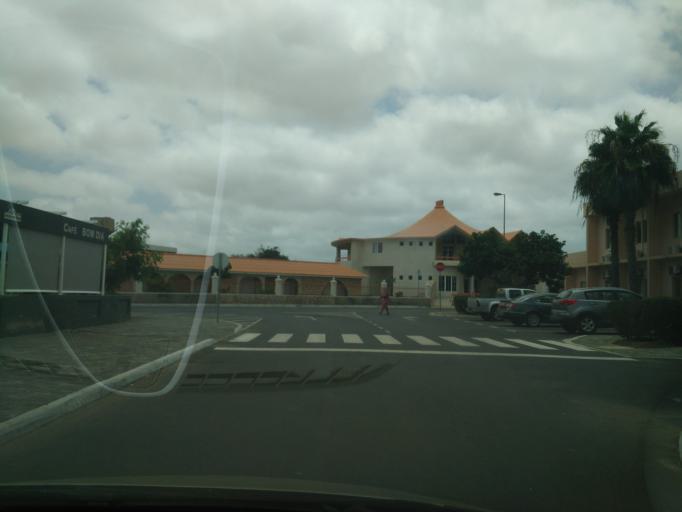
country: CV
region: Sal
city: Espargos
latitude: 16.7538
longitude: -22.9446
